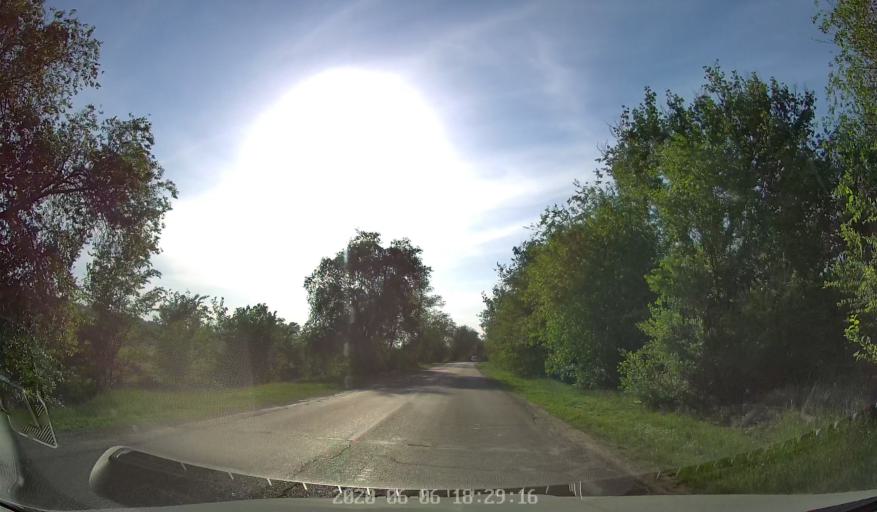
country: MD
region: Chisinau
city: Ciorescu
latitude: 47.1319
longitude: 28.9721
